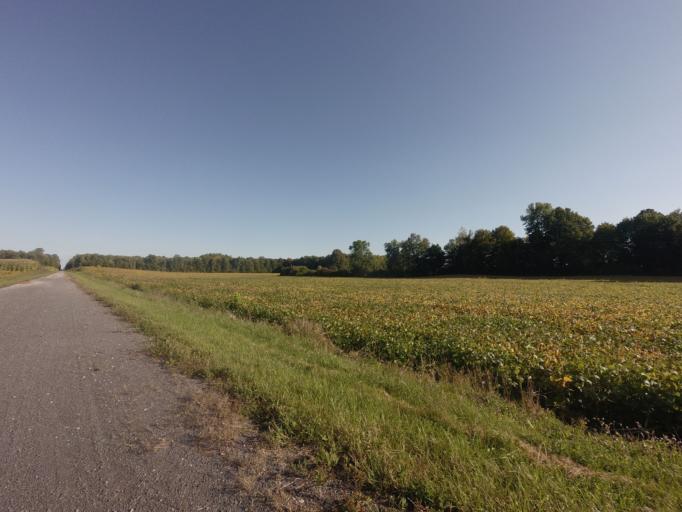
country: CA
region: Ontario
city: Hawkesbury
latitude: 45.5310
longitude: -74.5728
